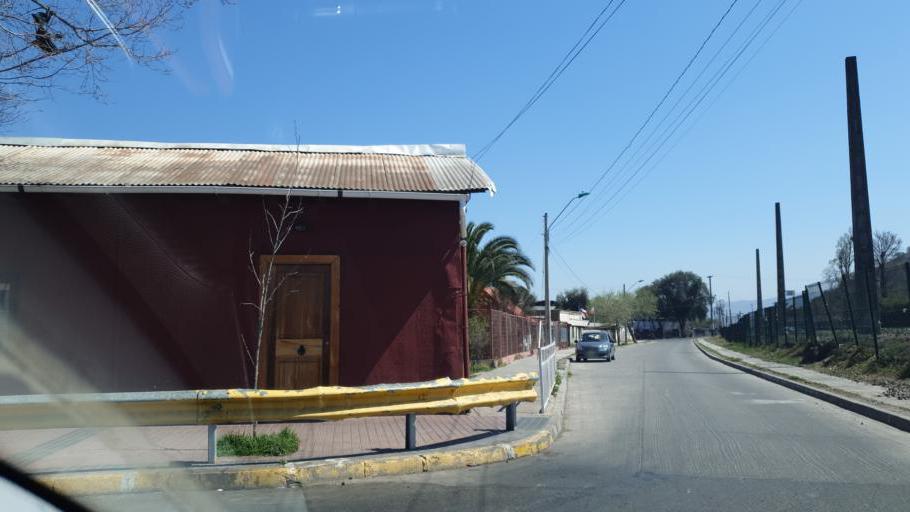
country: CL
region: Santiago Metropolitan
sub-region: Provincia de Talagante
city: Talagante
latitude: -33.6606
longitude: -70.9311
